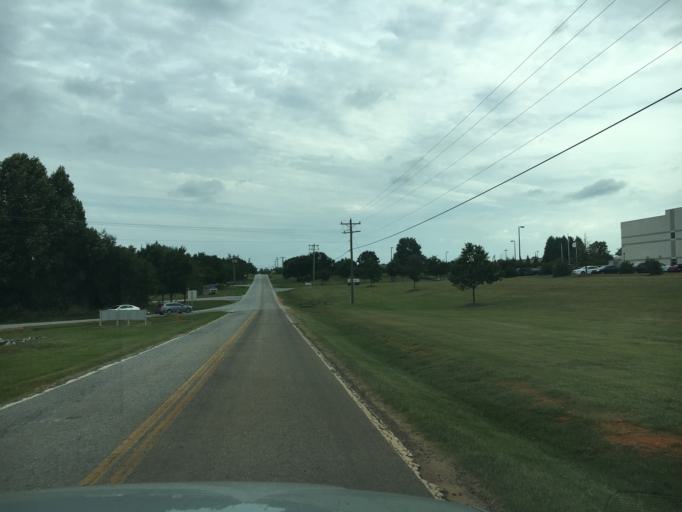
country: US
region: South Carolina
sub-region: Spartanburg County
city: Duncan
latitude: 34.9127
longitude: -82.1640
